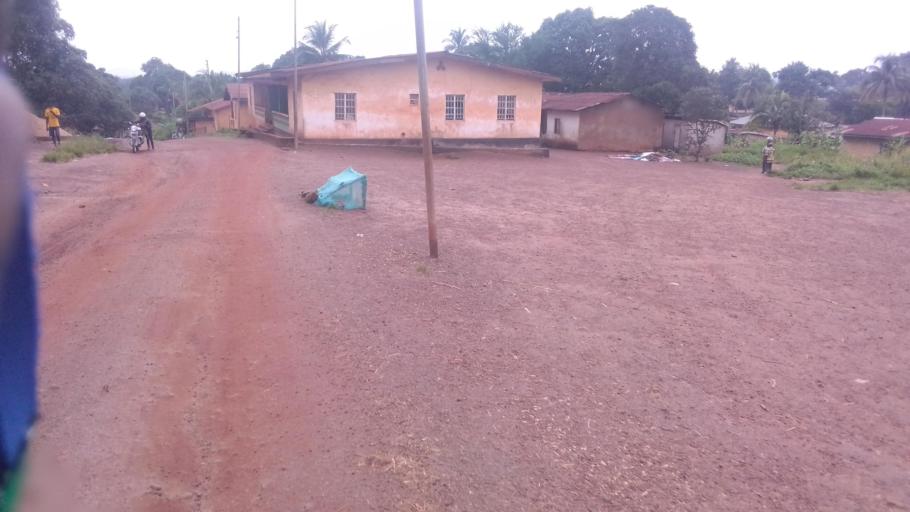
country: SL
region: Eastern Province
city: Kenema
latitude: 7.8714
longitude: -11.1791
